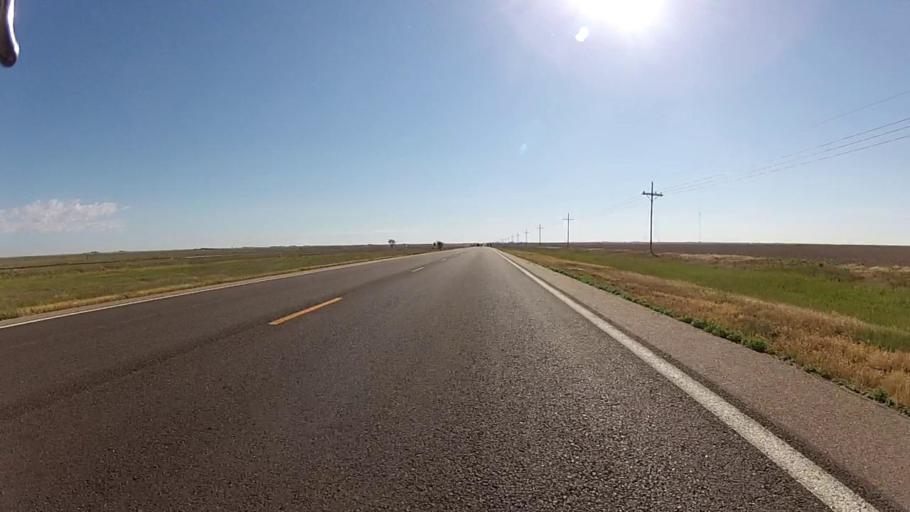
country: US
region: Kansas
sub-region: Haskell County
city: Sublette
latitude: 37.5574
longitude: -100.5775
